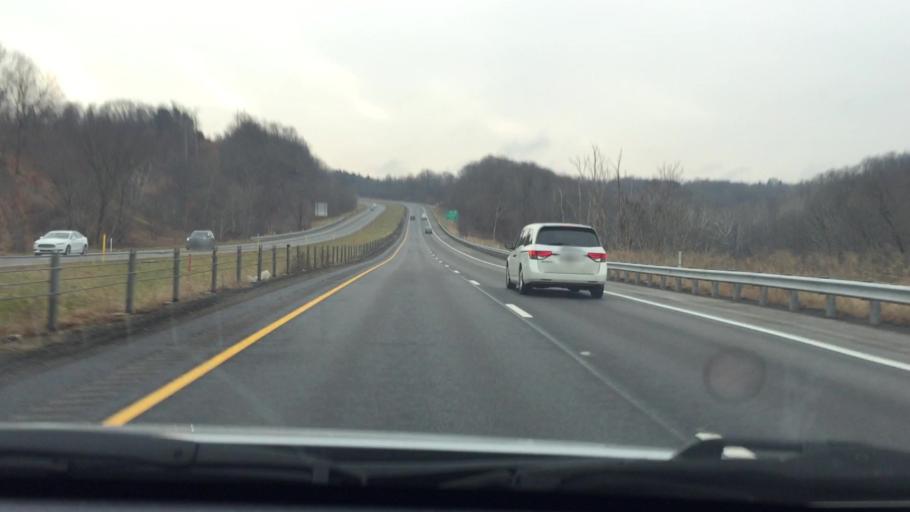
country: US
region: Pennsylvania
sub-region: Beaver County
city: Beaver
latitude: 40.6574
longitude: -80.3240
